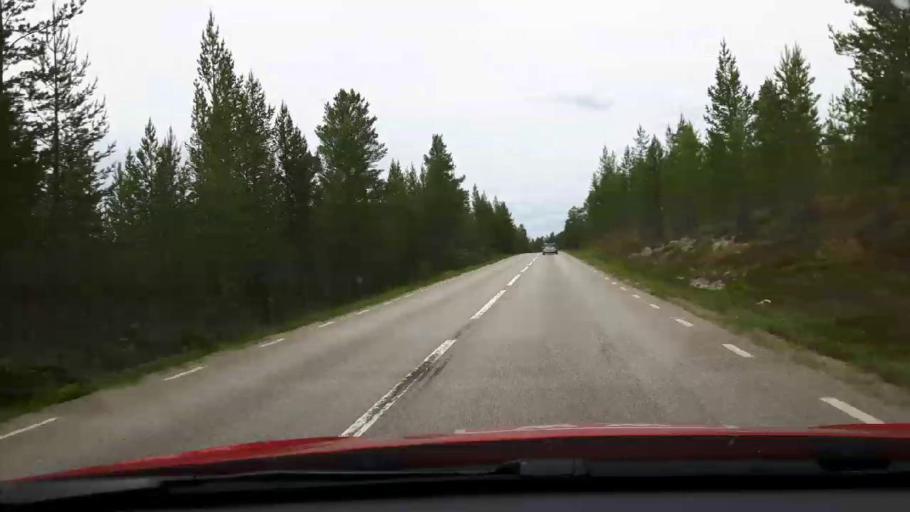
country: SE
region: Jaemtland
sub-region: Harjedalens Kommun
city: Sveg
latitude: 62.2334
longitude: 13.8549
